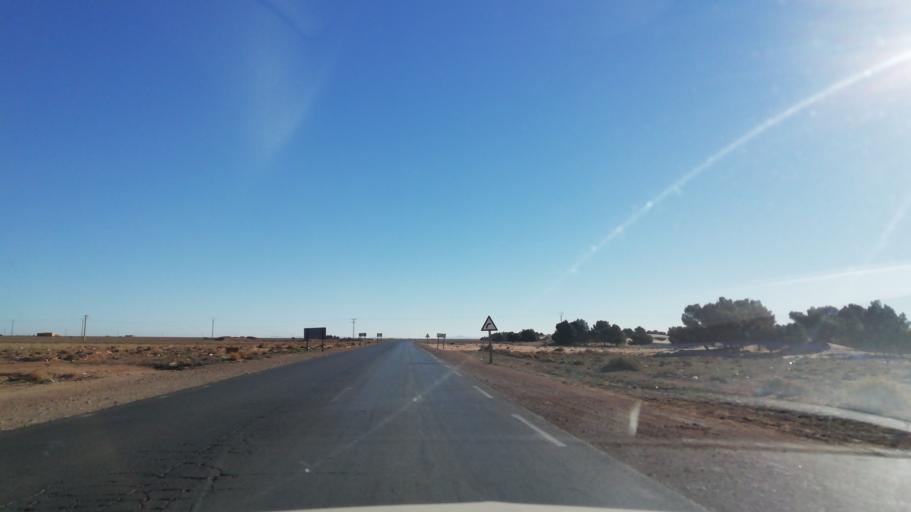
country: DZ
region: El Bayadh
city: El Bayadh
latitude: 33.8523
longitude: 0.6524
